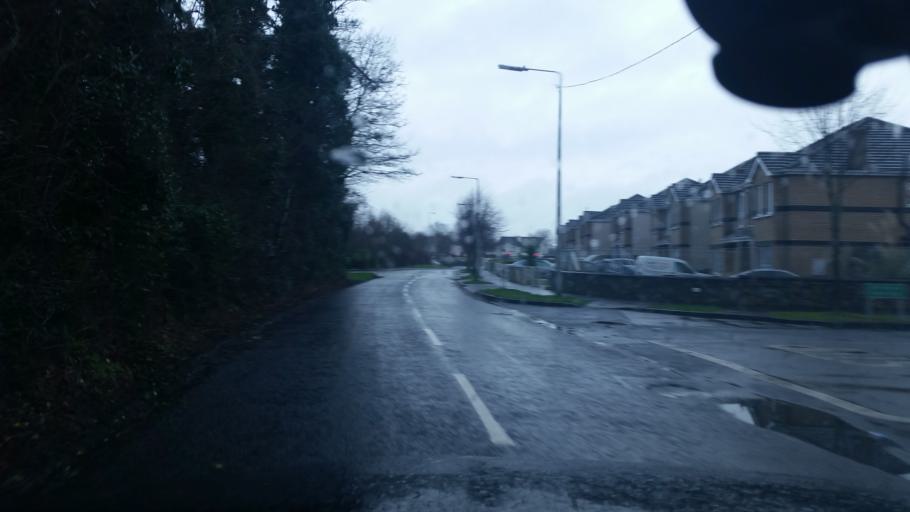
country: IE
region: Leinster
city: Hartstown
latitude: 53.3855
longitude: -6.4099
